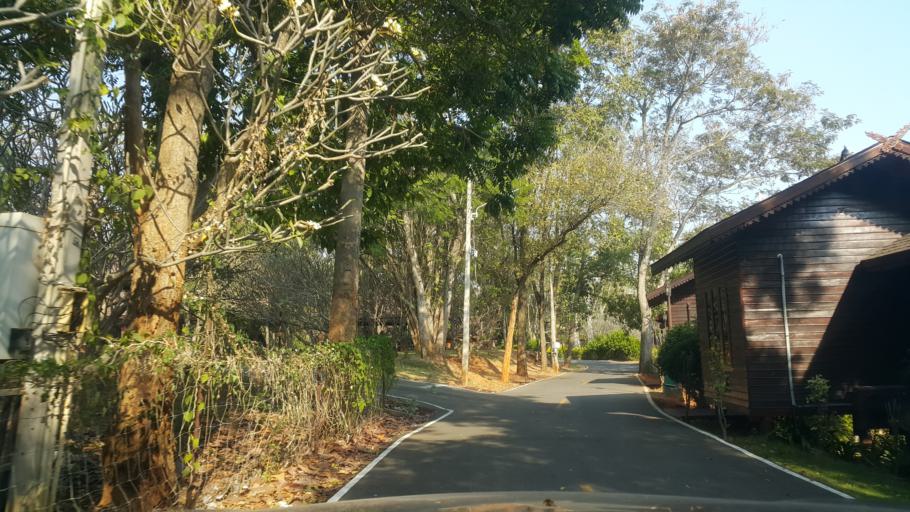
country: TH
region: Nakhon Ratchasima
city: Nakhon Ratchasima
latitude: 14.8520
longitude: 102.0760
